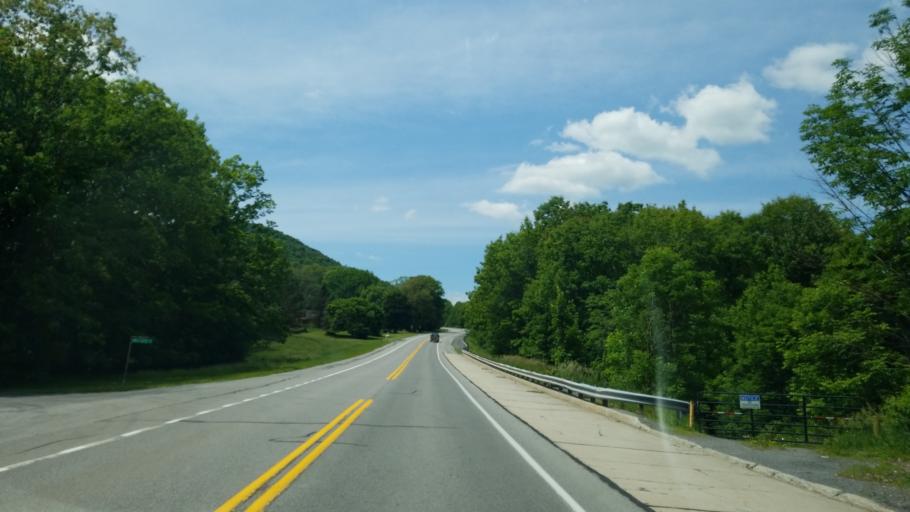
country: US
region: Pennsylvania
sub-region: Blair County
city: Tyrone
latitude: 40.6896
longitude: -78.2732
